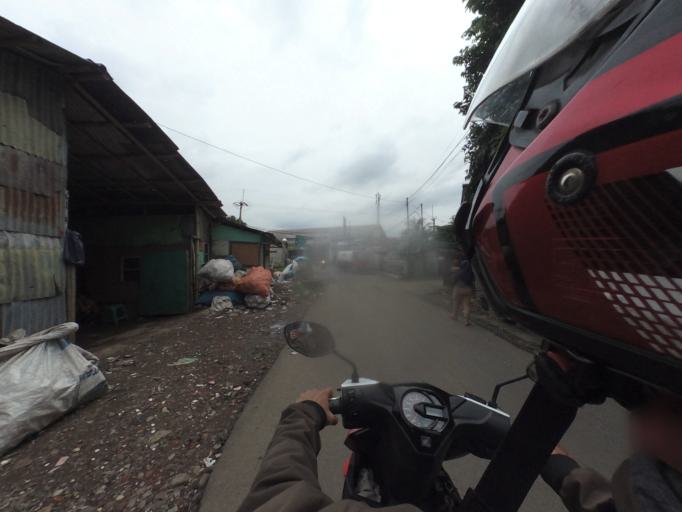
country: ID
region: West Java
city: Bogor
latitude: -6.6062
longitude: 106.7586
